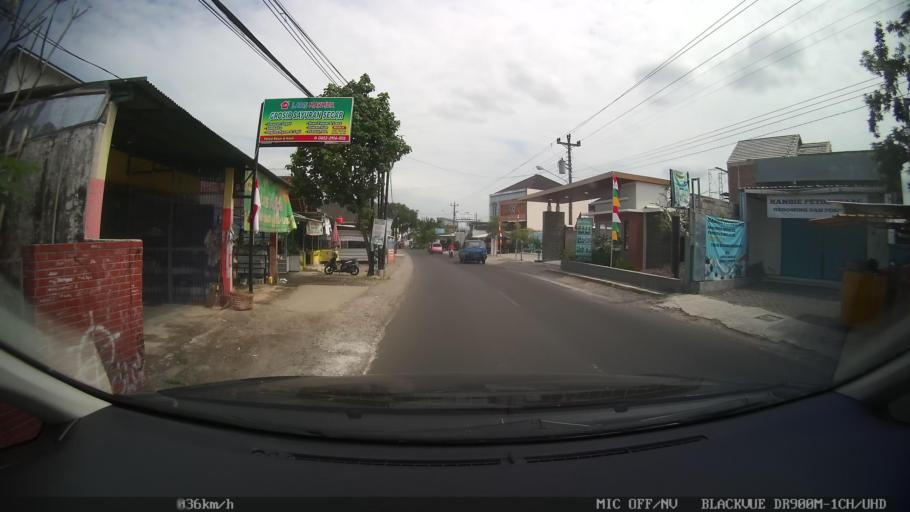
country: ID
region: Daerah Istimewa Yogyakarta
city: Depok
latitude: -7.7403
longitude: 110.4517
